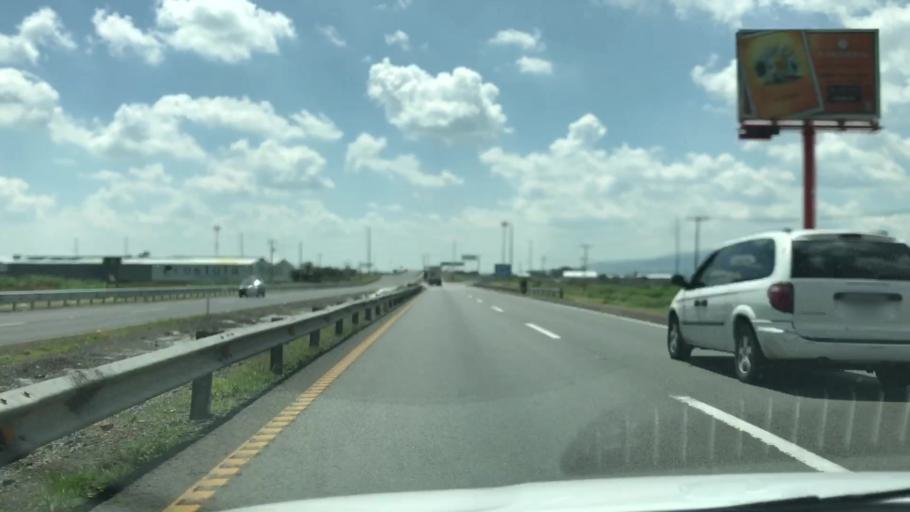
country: MX
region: Guanajuato
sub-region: Irapuato
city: Las Huertas Tercera Seccion
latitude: 20.6496
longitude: -101.3687
